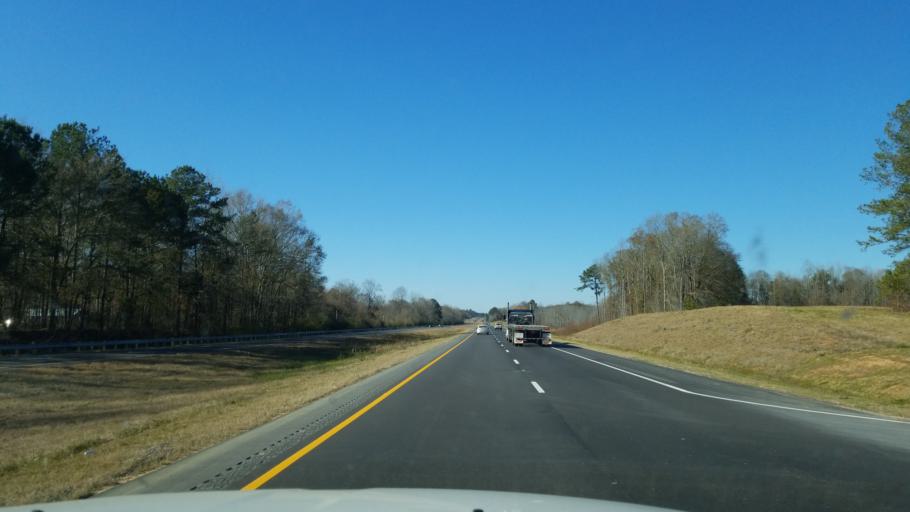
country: US
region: Alabama
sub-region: Pickens County
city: Gordo
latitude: 33.3434
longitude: -87.9441
